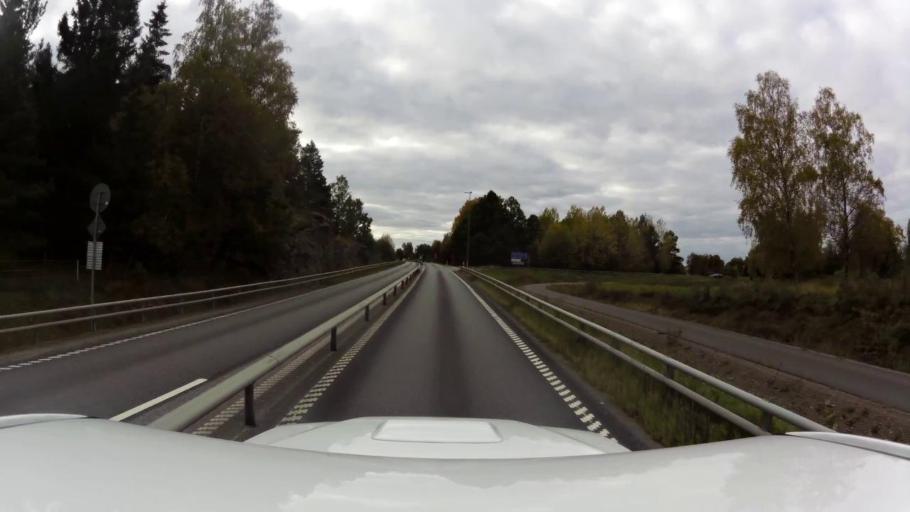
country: SE
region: OEstergoetland
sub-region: Linkopings Kommun
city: Malmslatt
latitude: 58.3038
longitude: 15.5642
